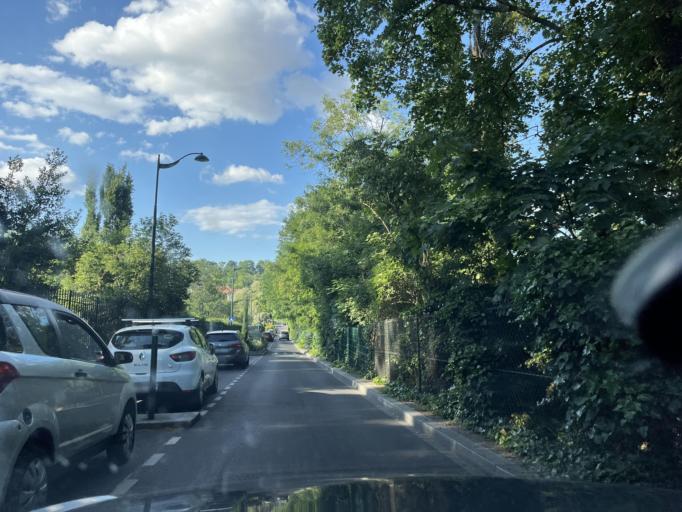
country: FR
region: Ile-de-France
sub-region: Departement des Hauts-de-Seine
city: Le Plessis-Robinson
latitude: 48.7838
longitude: 2.2716
